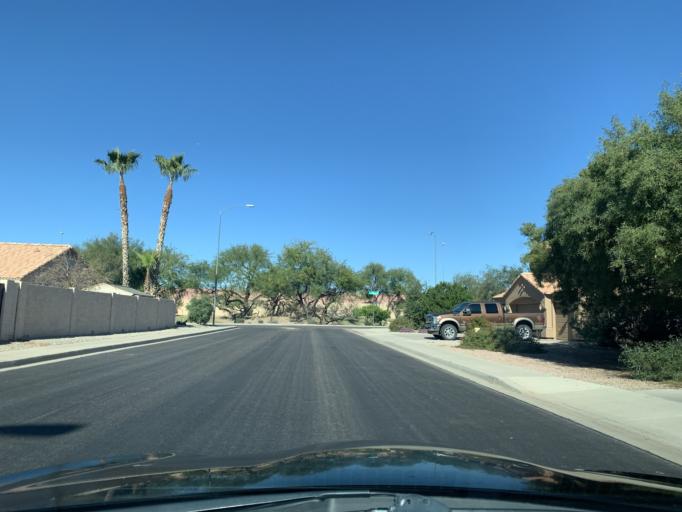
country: US
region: Arizona
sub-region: Pinal County
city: Apache Junction
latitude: 33.3851
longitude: -111.6265
